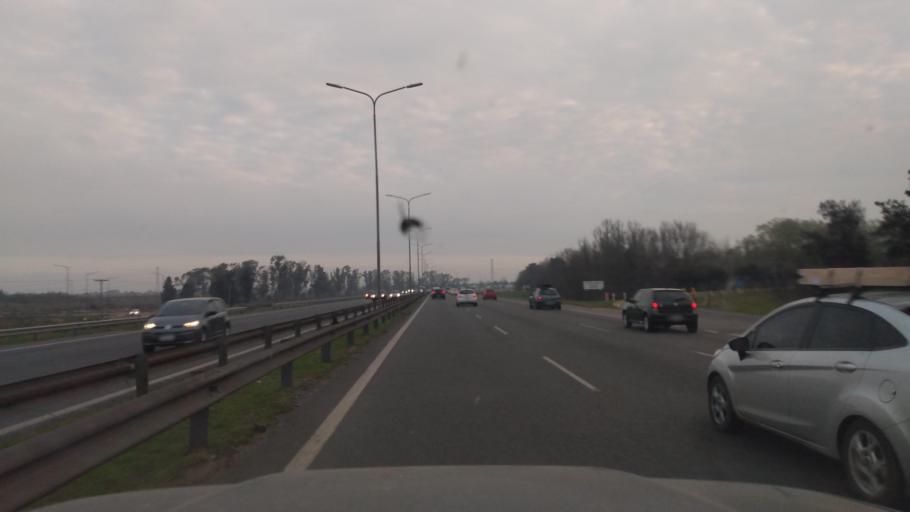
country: AR
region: Buenos Aires
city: Hurlingham
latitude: -34.5440
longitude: -58.6025
